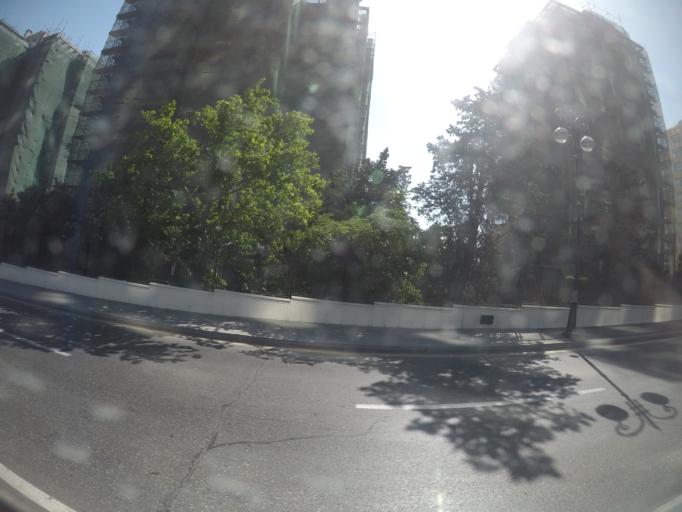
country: AZ
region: Baki
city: Badamdar
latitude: 40.3611
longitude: 49.8269
